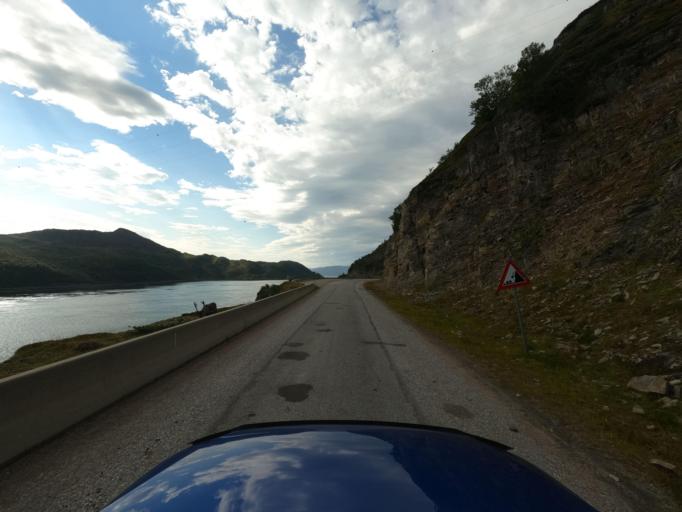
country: NO
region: Finnmark Fylke
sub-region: Kvalsund
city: Kvalsund
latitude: 70.5141
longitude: 23.9368
